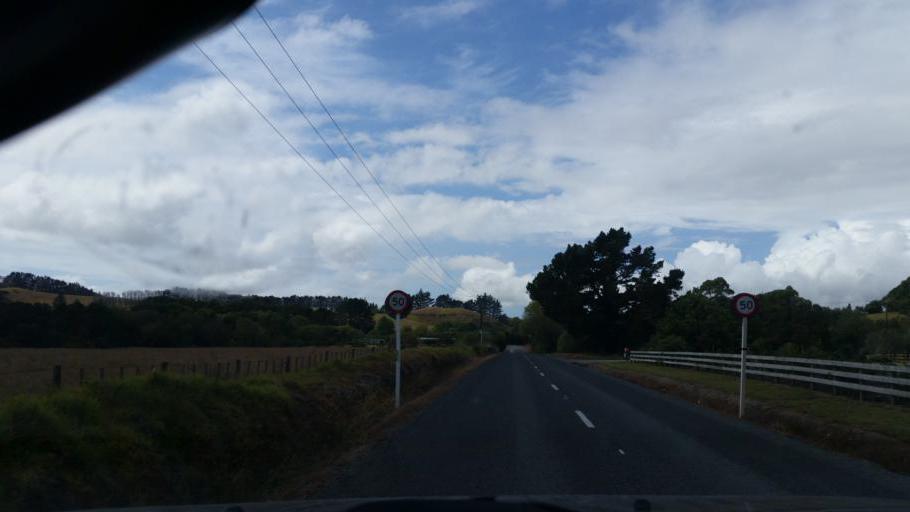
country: NZ
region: Auckland
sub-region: Auckland
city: Wellsford
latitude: -36.1223
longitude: 174.5537
